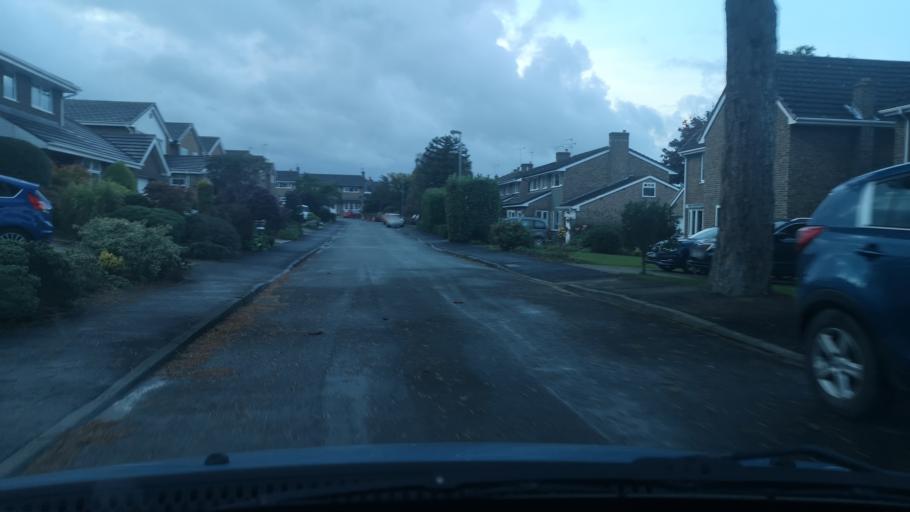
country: GB
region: England
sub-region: City and Borough of Wakefield
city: Low Ackworth
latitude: 53.6457
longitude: -1.3438
